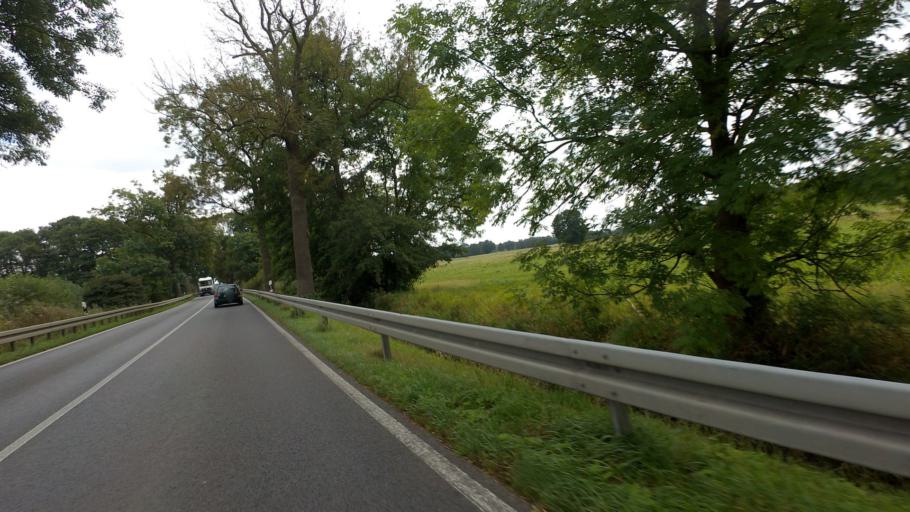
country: DE
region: Brandenburg
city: Golssen
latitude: 51.9626
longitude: 13.6216
